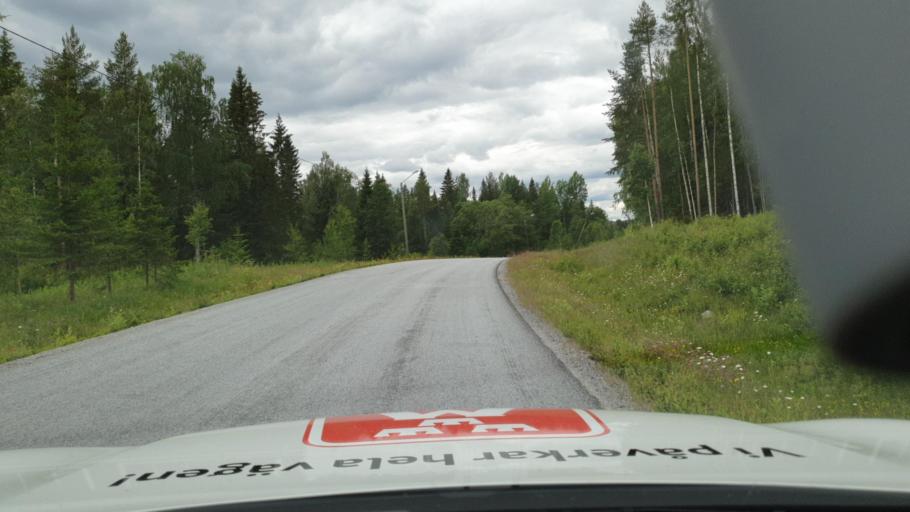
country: SE
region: Vaesterbotten
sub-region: Bjurholms Kommun
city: Bjurholm
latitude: 63.7819
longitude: 19.2134
